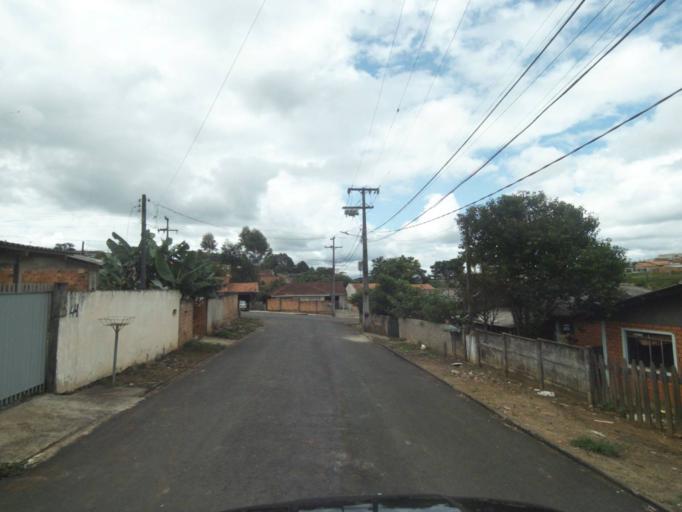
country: BR
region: Parana
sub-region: Telemaco Borba
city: Telemaco Borba
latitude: -24.3171
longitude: -50.6461
